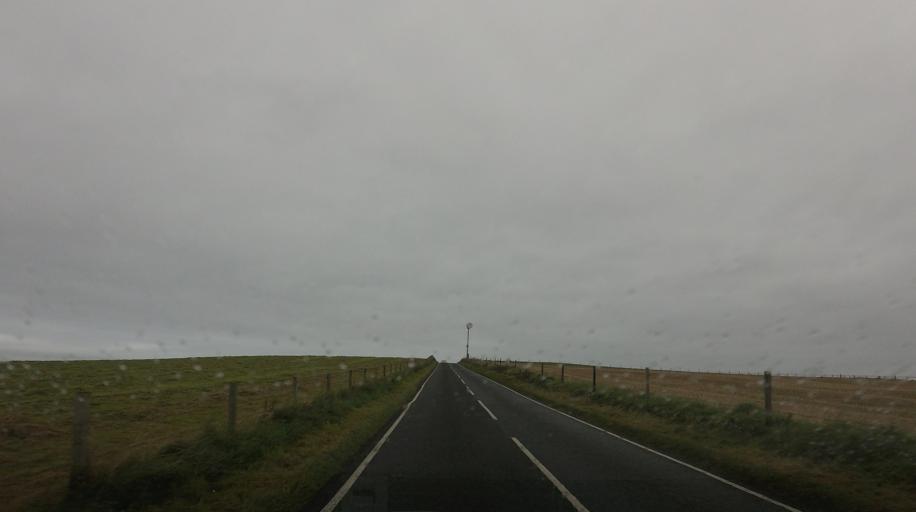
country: GB
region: Scotland
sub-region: Orkney Islands
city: Stromness
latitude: 59.1286
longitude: -3.3024
